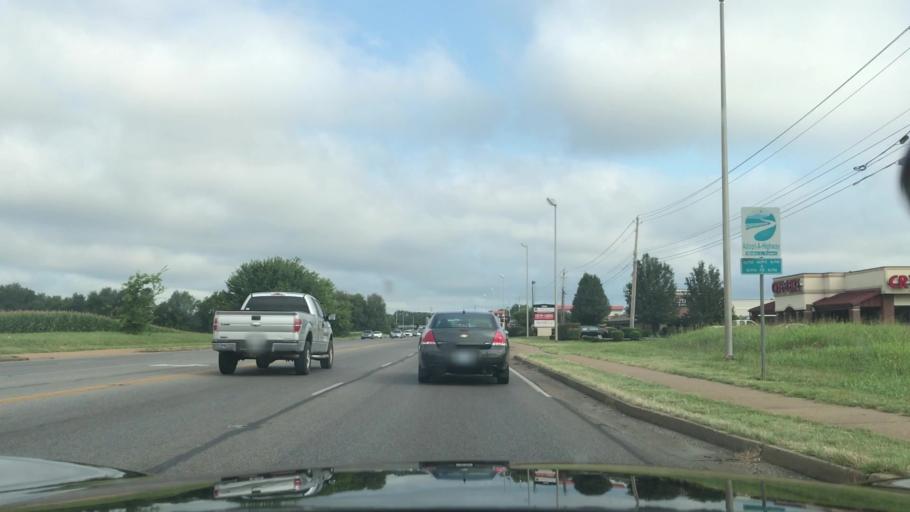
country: US
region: Kentucky
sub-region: Warren County
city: Bowling Green
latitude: 36.9574
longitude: -86.4479
